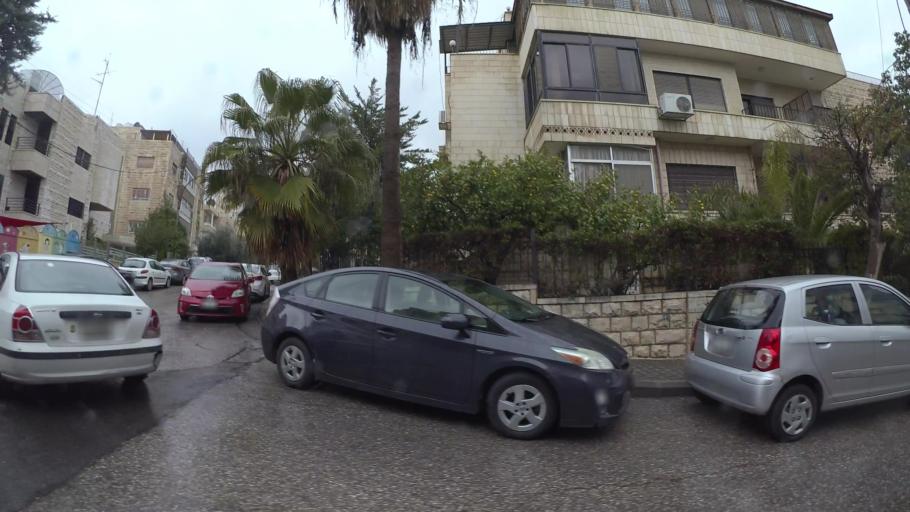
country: JO
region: Amman
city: Amman
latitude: 31.9623
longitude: 35.9012
